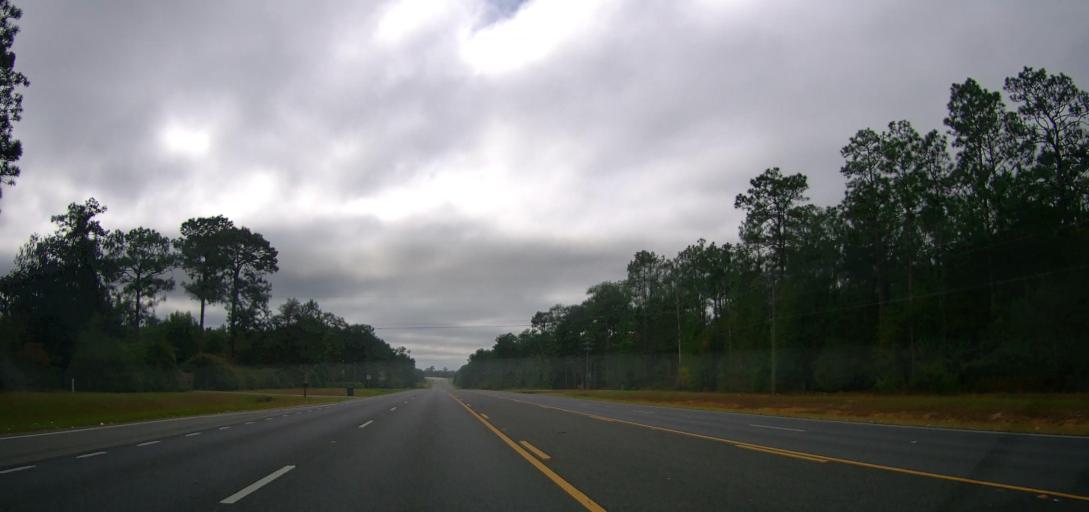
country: US
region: Georgia
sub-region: Colquitt County
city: Moultrie
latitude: 31.0877
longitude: -83.8107
